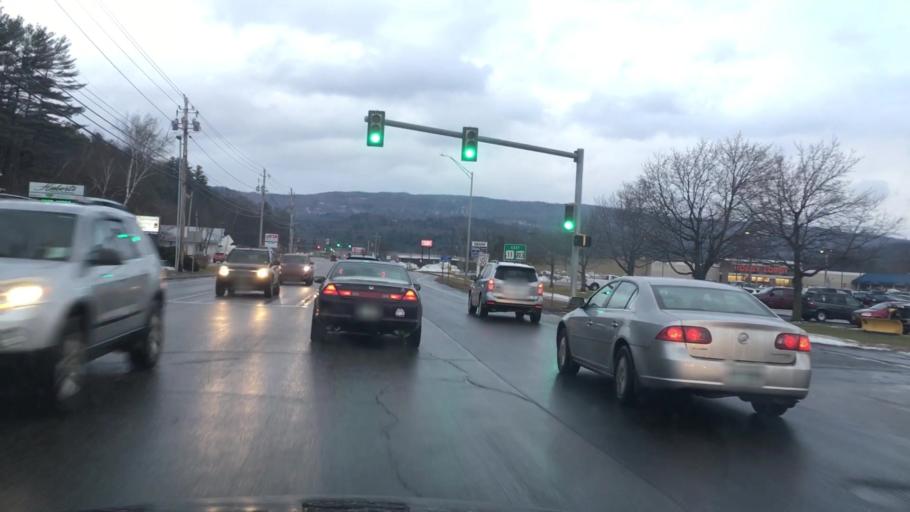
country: US
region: New Hampshire
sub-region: Sullivan County
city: Claremont
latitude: 43.3648
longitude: -72.3190
